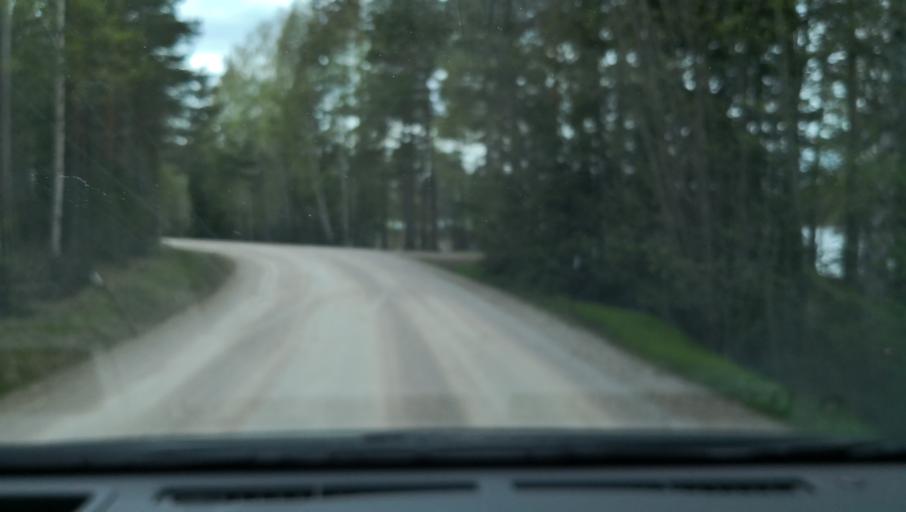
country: SE
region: Vaestmanland
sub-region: Norbergs Kommun
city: Norberg
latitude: 60.0917
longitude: 15.8573
